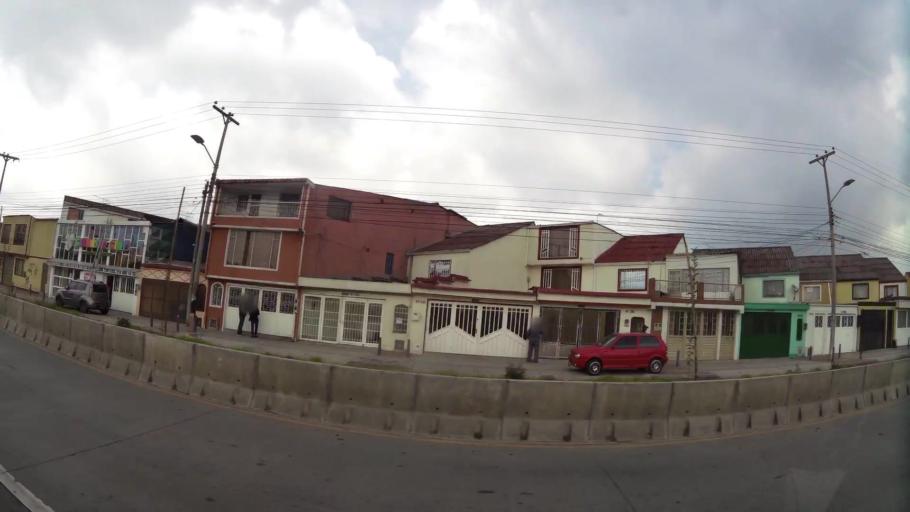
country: CO
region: Bogota D.C.
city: Bogota
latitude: 4.5894
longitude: -74.1283
